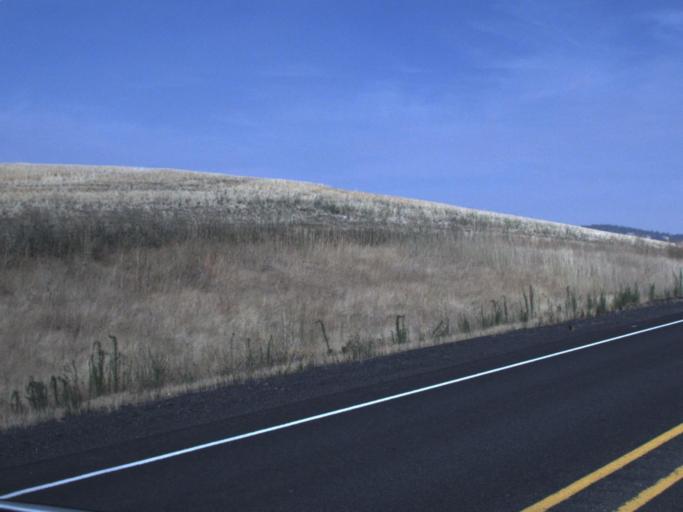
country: US
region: Washington
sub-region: Whitman County
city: Pullman
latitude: 46.8155
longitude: -117.1170
